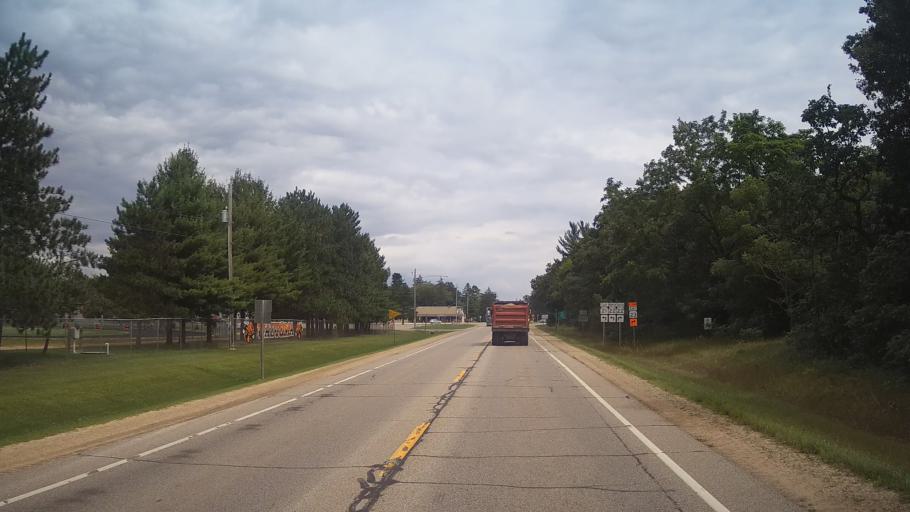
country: US
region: Wisconsin
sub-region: Waushara County
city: Wautoma
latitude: 44.0684
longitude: -89.3010
